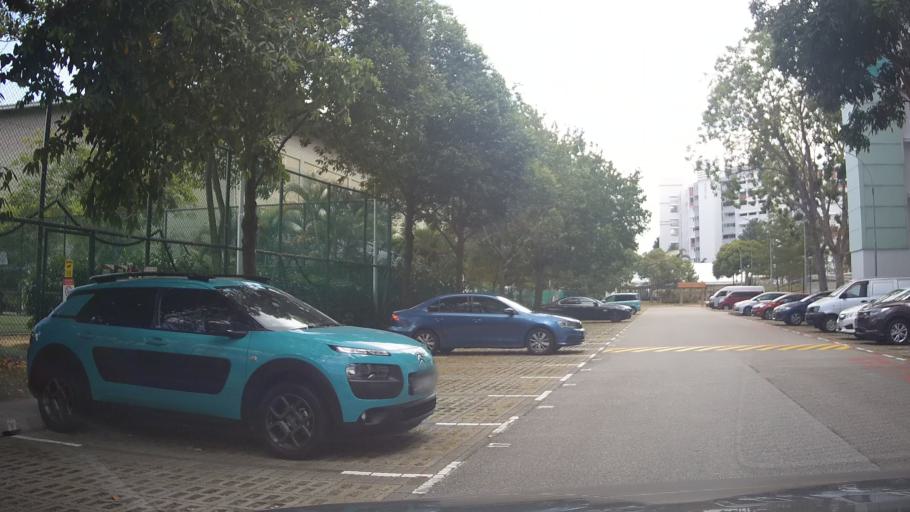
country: SG
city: Singapore
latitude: 1.3534
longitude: 103.9481
